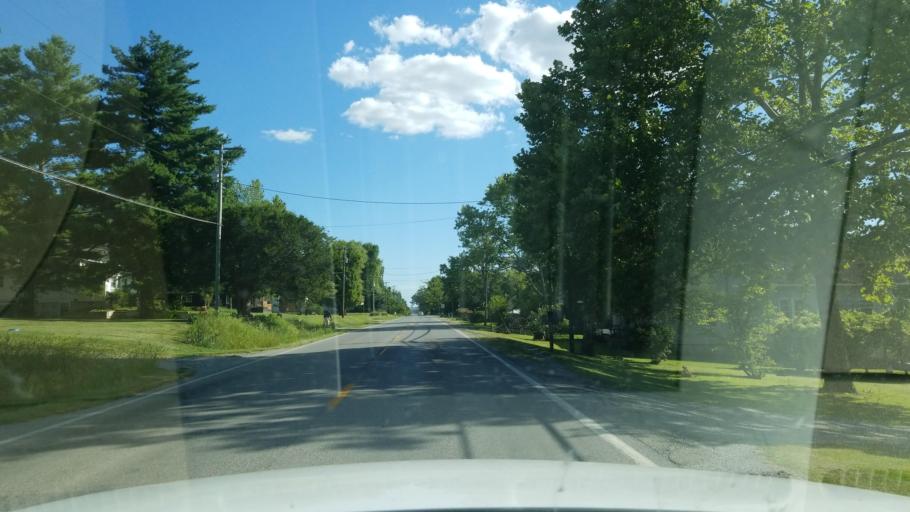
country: US
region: Illinois
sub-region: Saline County
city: Harrisburg
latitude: 37.7134
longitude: -88.5359
